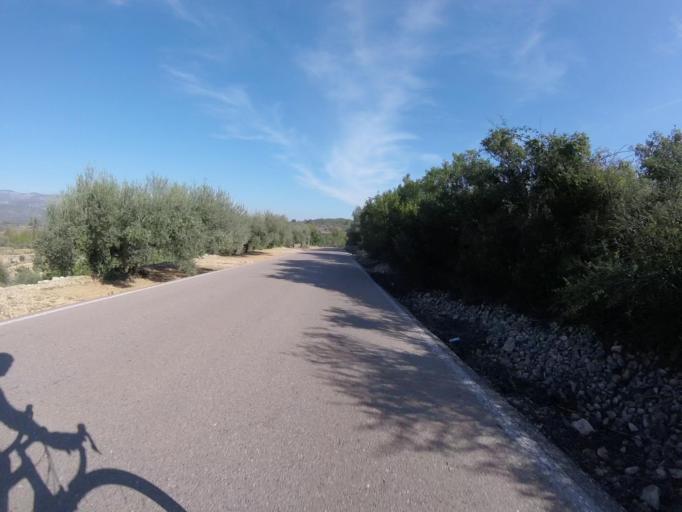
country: ES
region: Valencia
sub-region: Provincia de Castello
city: Benlloch
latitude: 40.2434
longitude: 0.0780
